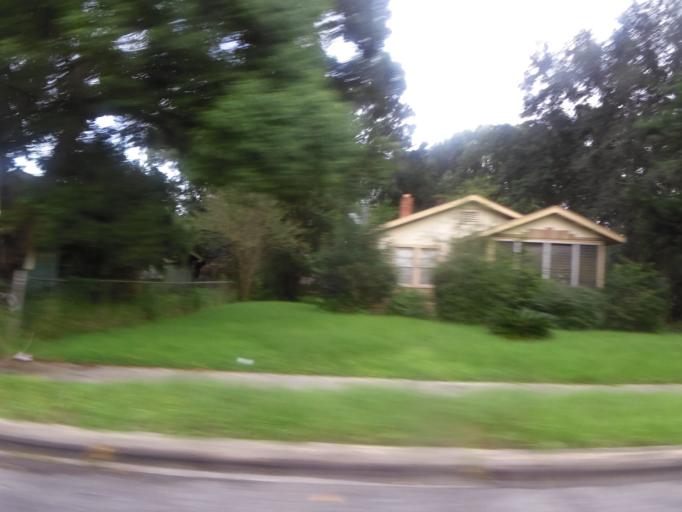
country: US
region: Florida
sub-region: Duval County
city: Jacksonville
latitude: 30.3507
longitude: -81.7229
